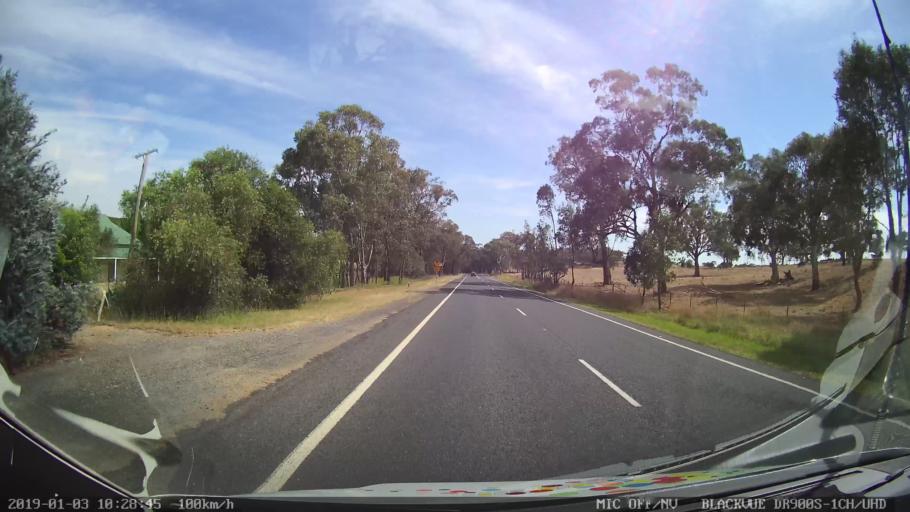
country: AU
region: New South Wales
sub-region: Young
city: Young
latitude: -34.3834
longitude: 148.2597
